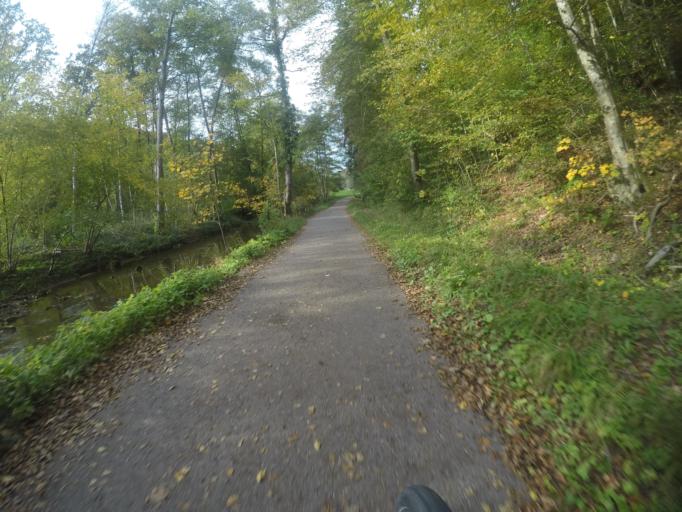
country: DE
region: Baden-Wuerttemberg
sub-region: Tuebingen Region
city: Tuebingen
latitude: 48.5443
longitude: 9.0767
